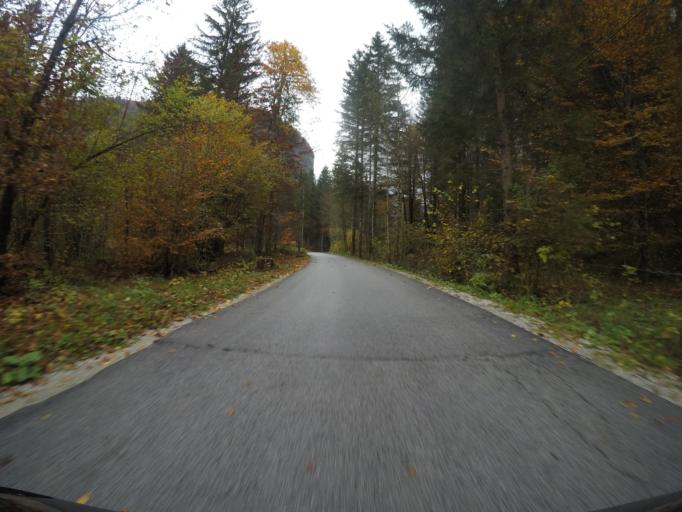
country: SI
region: Jesenice
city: Hrusica
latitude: 46.4138
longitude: 13.9926
